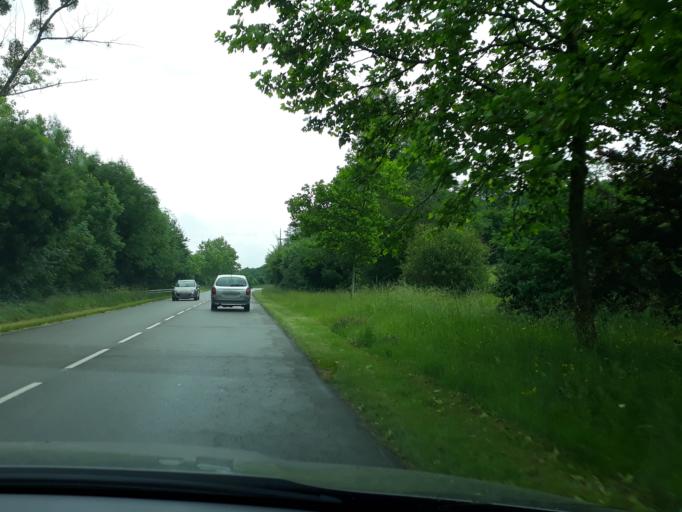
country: FR
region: Limousin
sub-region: Departement de la Correze
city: Cosnac
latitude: 45.1538
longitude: 1.6173
